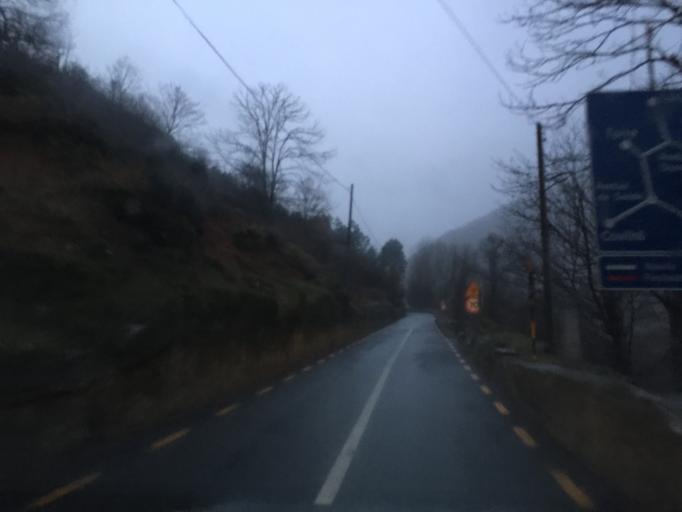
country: PT
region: Guarda
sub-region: Manteigas
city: Manteigas
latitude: 40.3817
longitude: -7.5441
